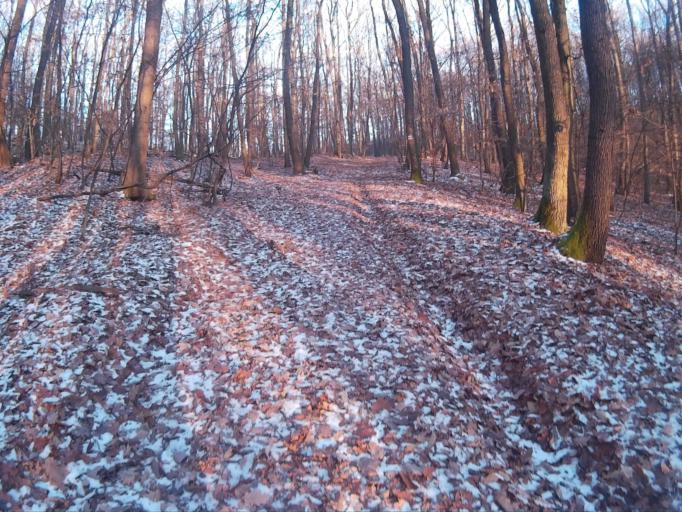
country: HU
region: Borsod-Abauj-Zemplen
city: Putnok
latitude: 48.3338
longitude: 20.4273
